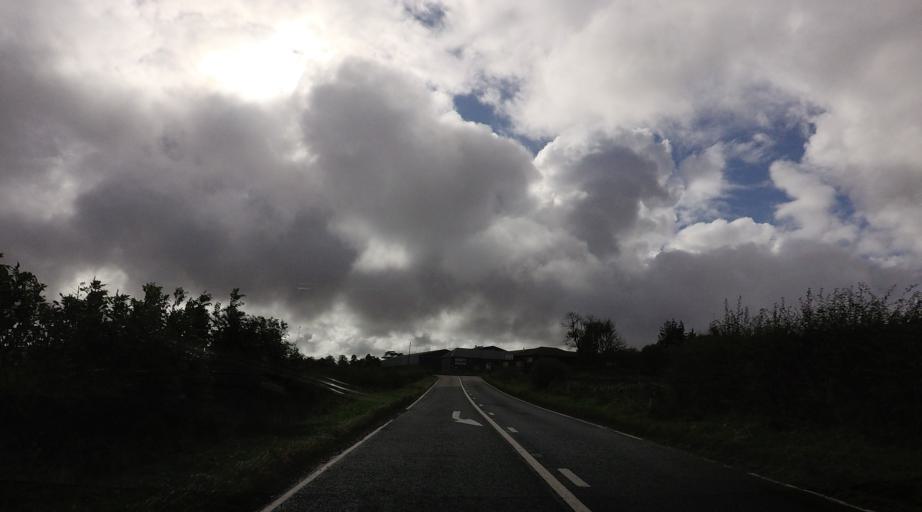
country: GB
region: Scotland
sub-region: Fife
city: Balmullo
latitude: 56.3609
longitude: -2.9403
